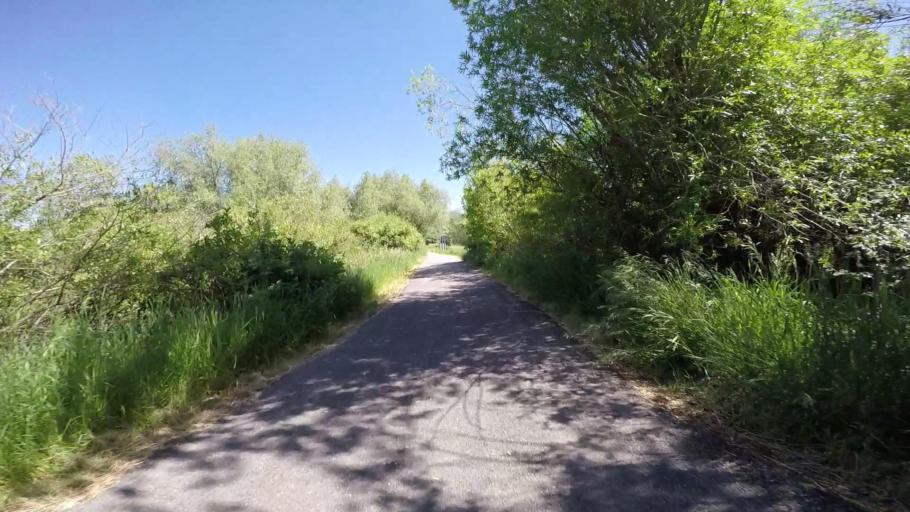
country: US
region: Utah
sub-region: Summit County
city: Park City
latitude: 40.6630
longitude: -111.5112
